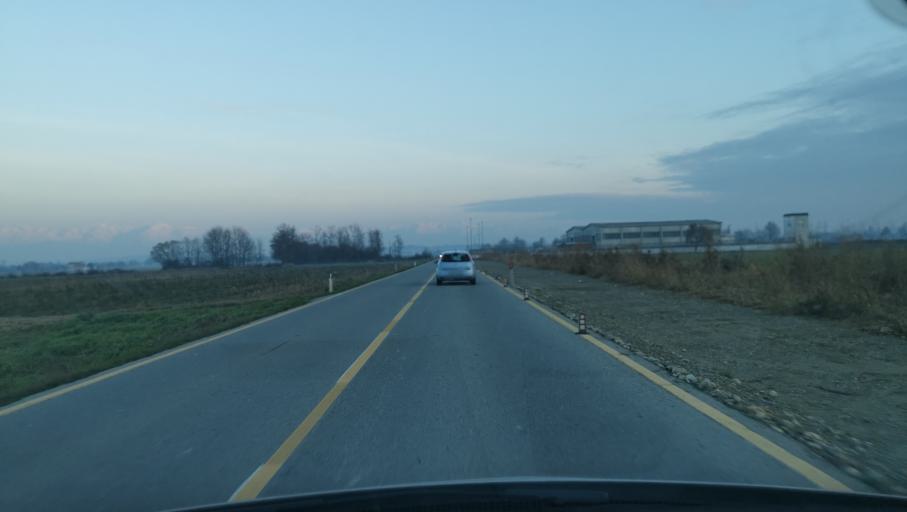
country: IT
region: Piedmont
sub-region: Provincia di Torino
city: Caluso
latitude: 45.2593
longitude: 7.8920
